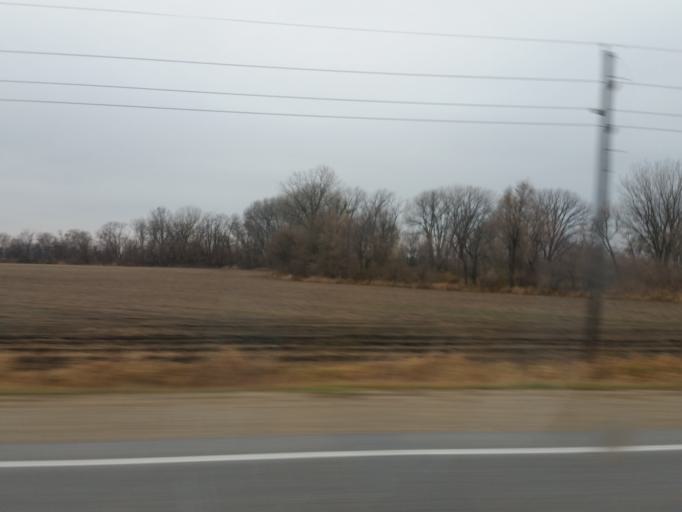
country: US
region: Iowa
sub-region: Black Hawk County
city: Elk Run Heights
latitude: 42.4052
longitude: -92.2613
